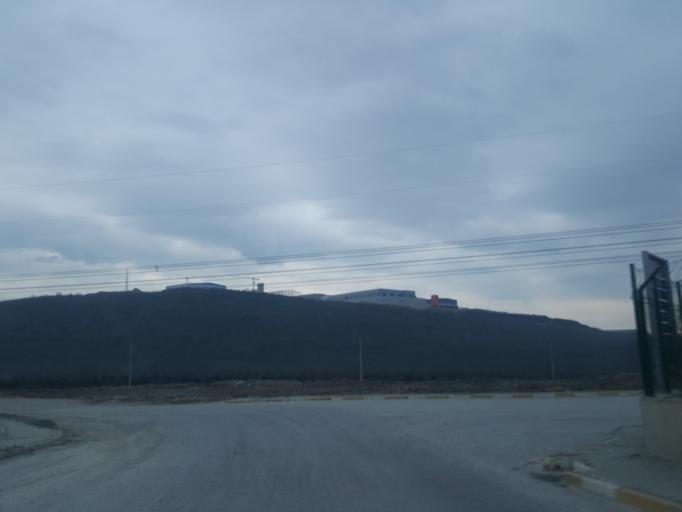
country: TR
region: Kocaeli
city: Tavsanli
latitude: 40.8596
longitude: 29.5712
